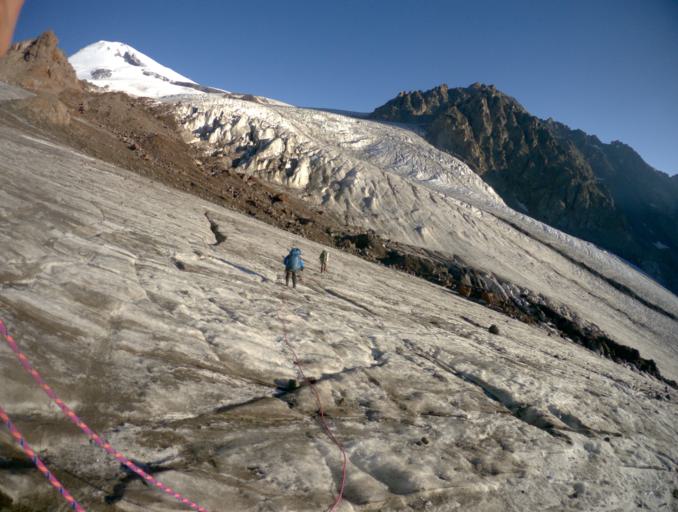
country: RU
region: Kabardino-Balkariya
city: Terskol
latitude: 43.3176
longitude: 42.5176
